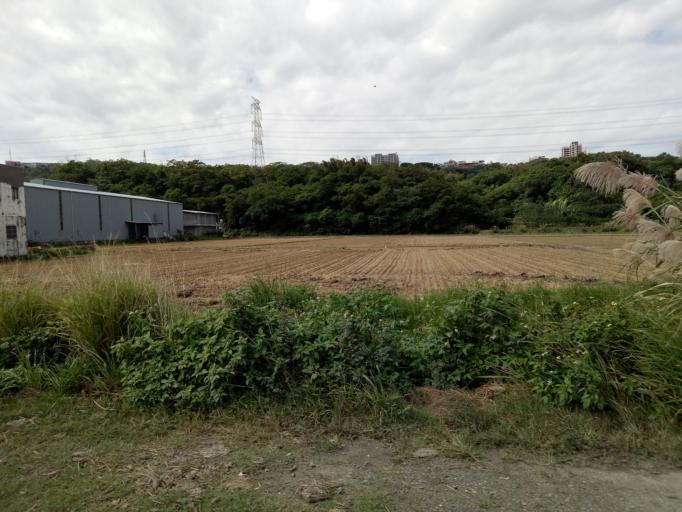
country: TW
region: Taiwan
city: Daxi
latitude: 24.9044
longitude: 121.2935
